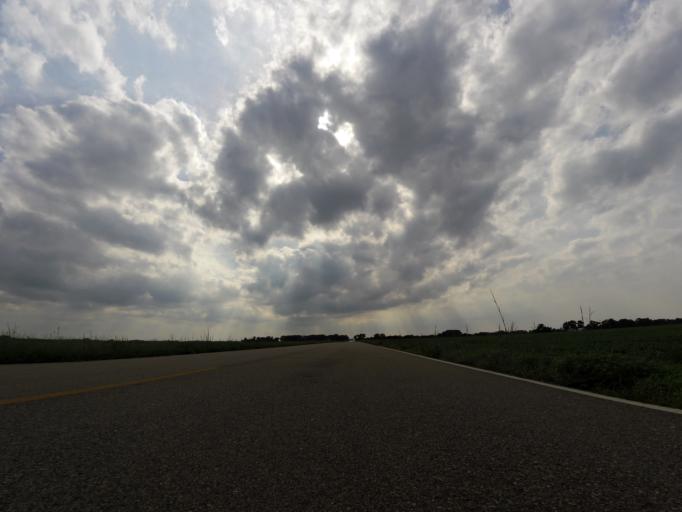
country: US
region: Kansas
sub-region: Reno County
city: South Hutchinson
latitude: 37.8976
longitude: -98.0528
